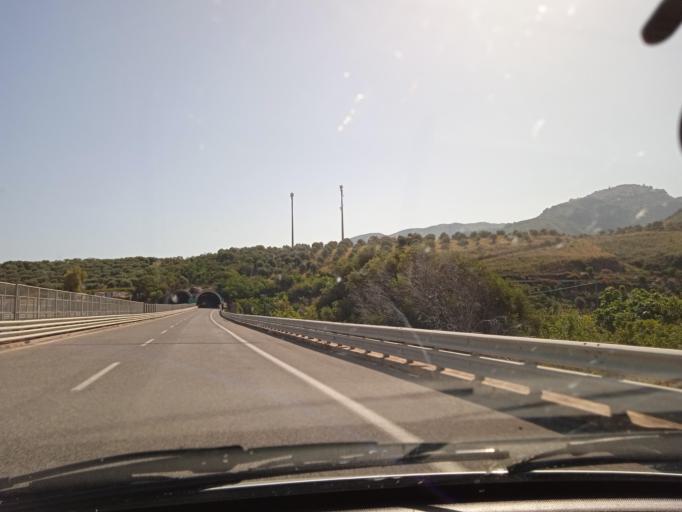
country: IT
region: Sicily
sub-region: Messina
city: Torrenova
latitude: 38.0786
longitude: 14.6666
